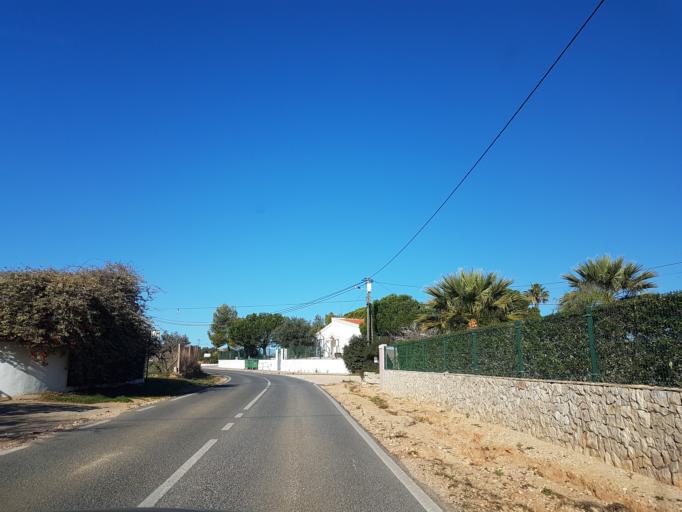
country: PT
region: Faro
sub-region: Lagoa
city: Carvoeiro
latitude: 37.0954
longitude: -8.4362
